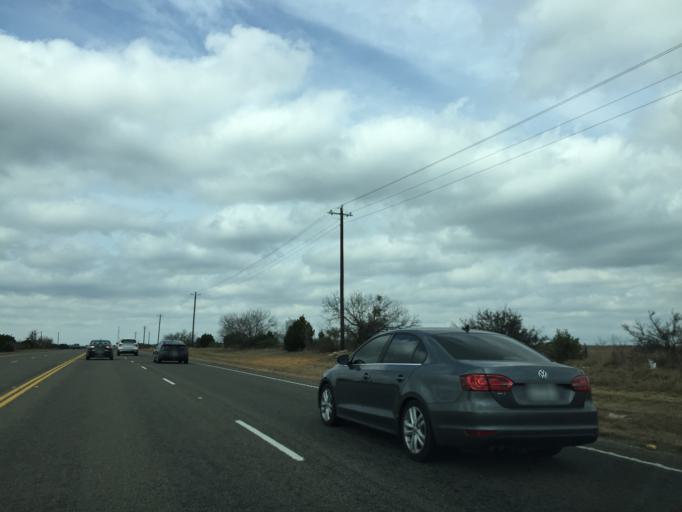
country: US
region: Texas
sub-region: Burnet County
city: Marble Falls
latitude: 30.4714
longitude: -98.1783
